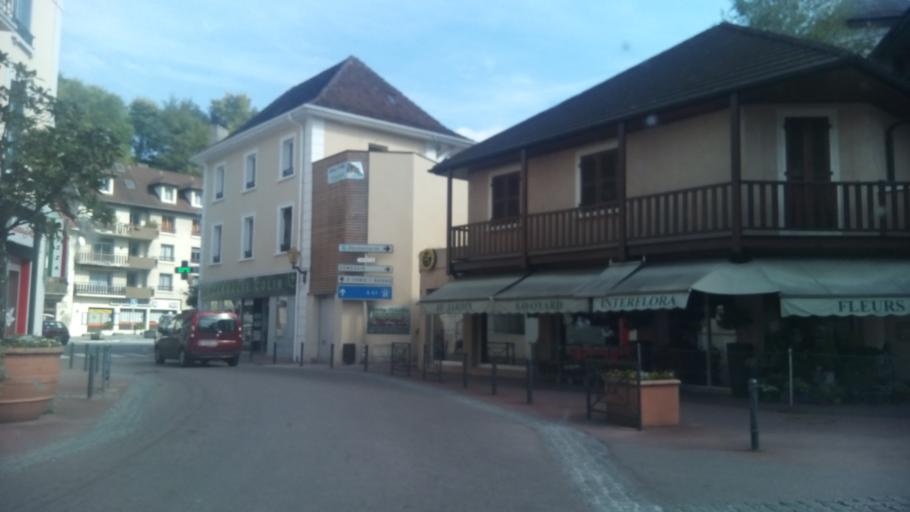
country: FR
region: Rhone-Alpes
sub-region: Departement de la Savoie
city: Le Pont-de-Beauvoisin
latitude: 45.5365
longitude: 5.6735
